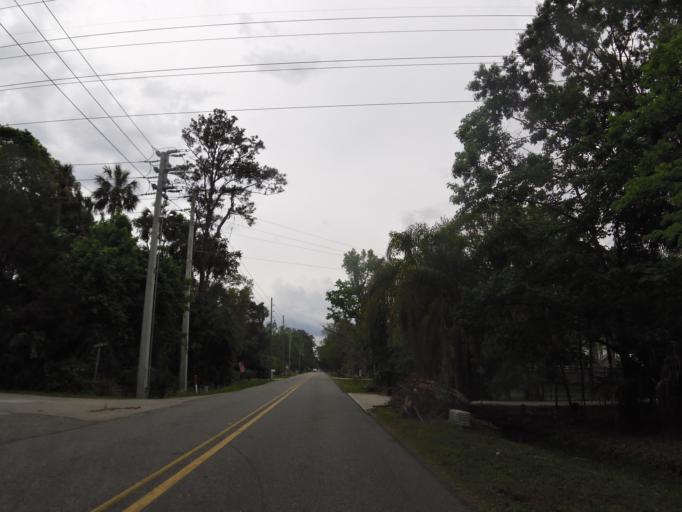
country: US
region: Florida
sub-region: Saint Johns County
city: Palm Valley
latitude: 30.1943
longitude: -81.4047
